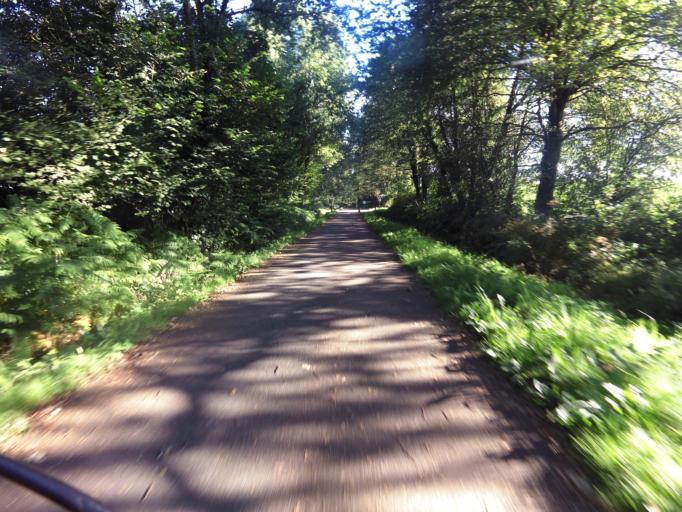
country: FR
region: Brittany
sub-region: Departement du Morbihan
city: Guillac
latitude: 47.8923
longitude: -2.4362
